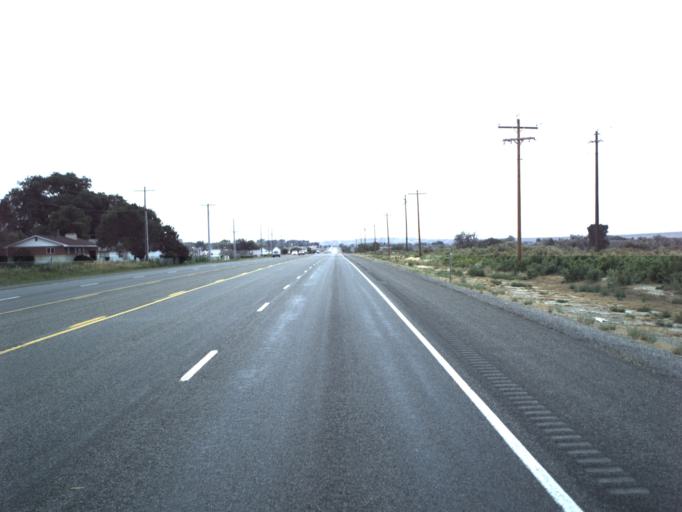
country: US
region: Utah
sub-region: Carbon County
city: Wellington
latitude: 39.5625
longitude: -110.7696
